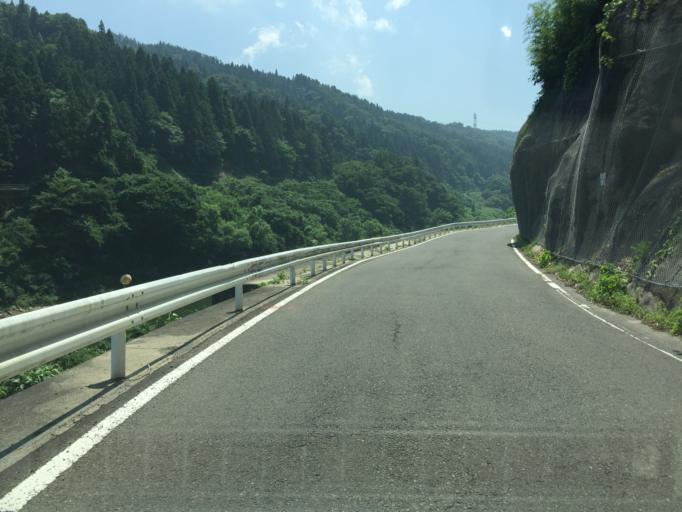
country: JP
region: Miyagi
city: Marumori
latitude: 37.9223
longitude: 140.6895
